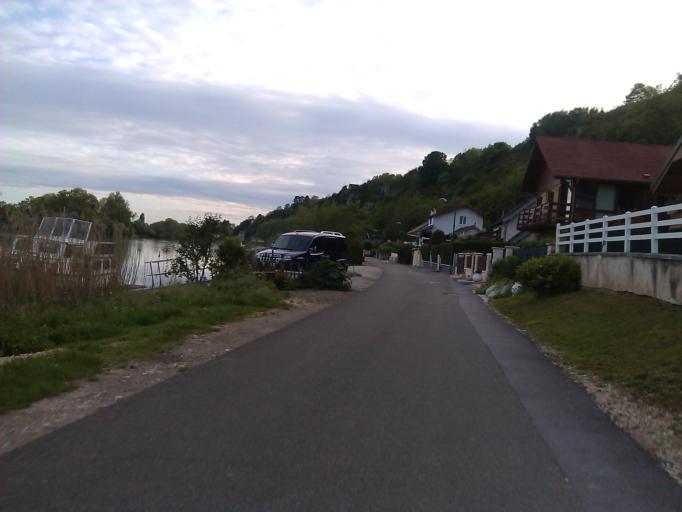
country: FR
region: Franche-Comte
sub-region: Departement du Jura
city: Dole
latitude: 47.1302
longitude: 5.5704
